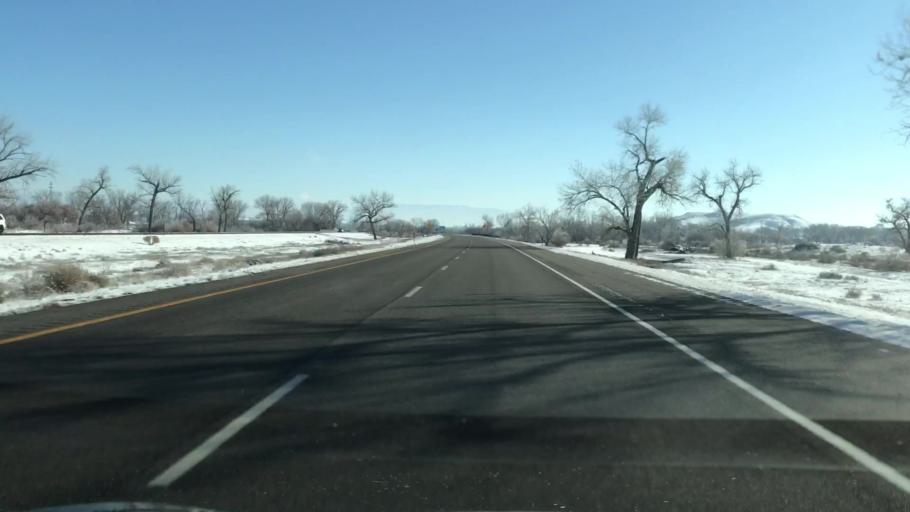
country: US
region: Colorado
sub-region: Mesa County
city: Loma
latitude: 39.1635
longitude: -108.7792
